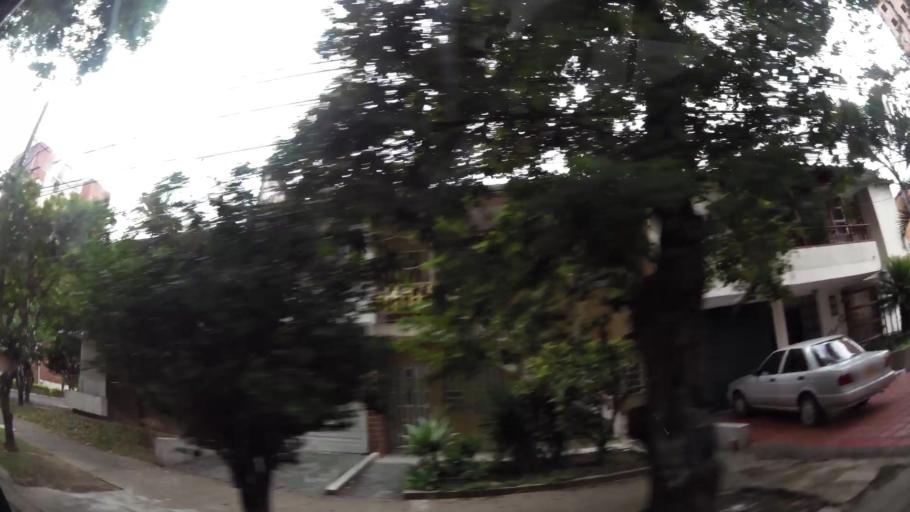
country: CO
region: Antioquia
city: Medellin
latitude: 6.2630
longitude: -75.6001
